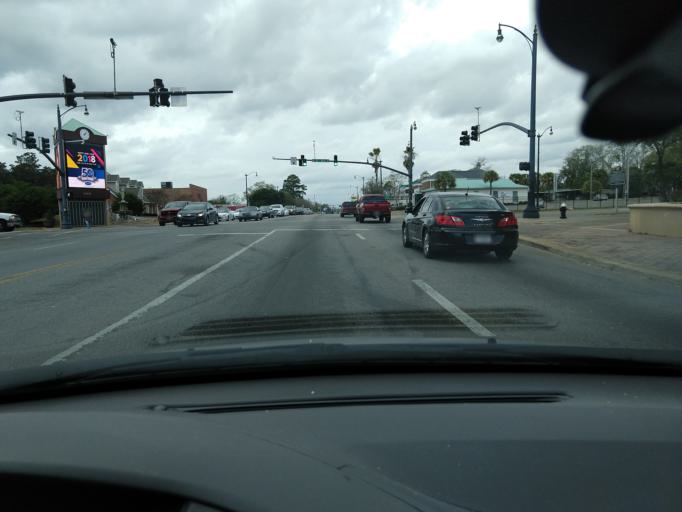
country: US
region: Alabama
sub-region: Houston County
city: Dothan
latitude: 31.2237
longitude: -85.3930
